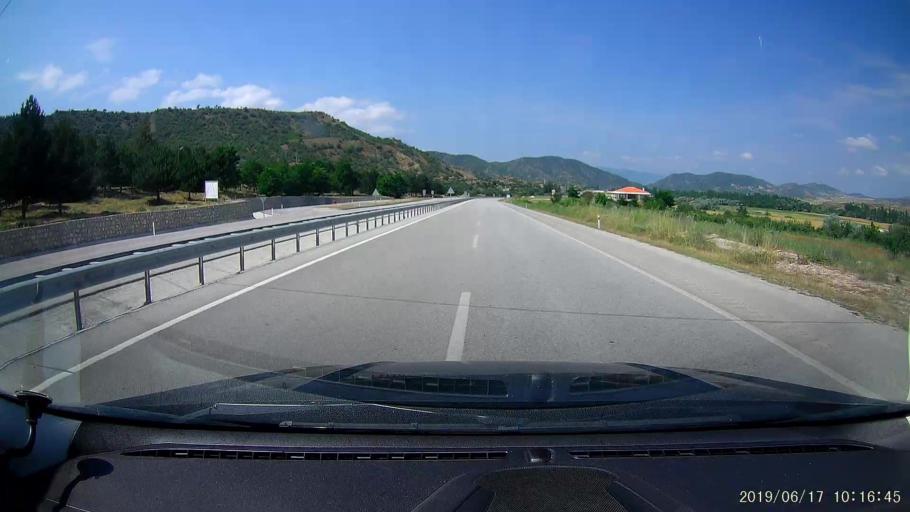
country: TR
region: Corum
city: Osmancik
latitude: 40.9870
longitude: 34.9675
